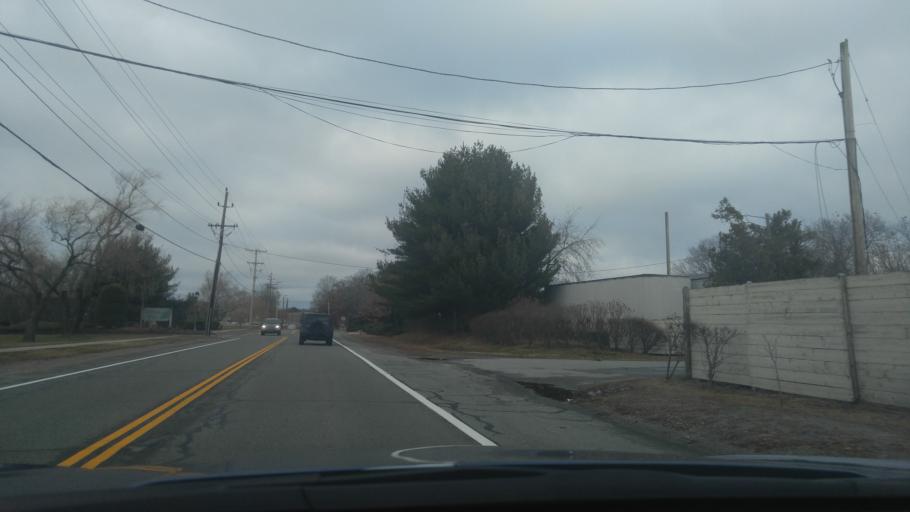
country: US
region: Rhode Island
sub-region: Kent County
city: Warwick
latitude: 41.7059
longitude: -71.3983
